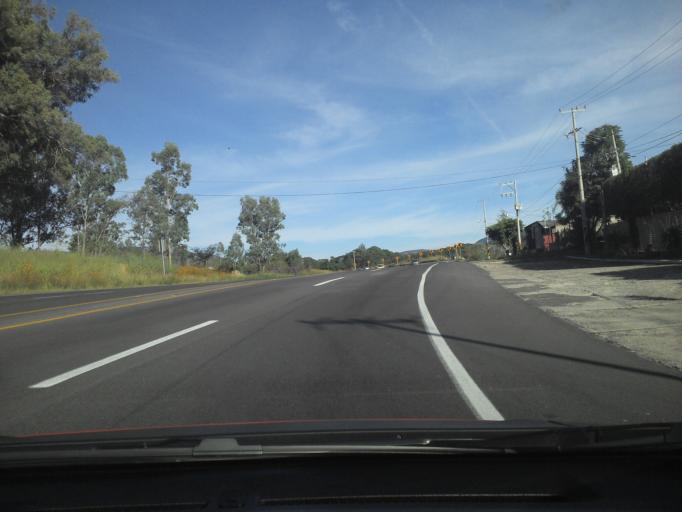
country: MX
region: Jalisco
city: La Venta del Astillero
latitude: 20.7279
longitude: -103.6178
